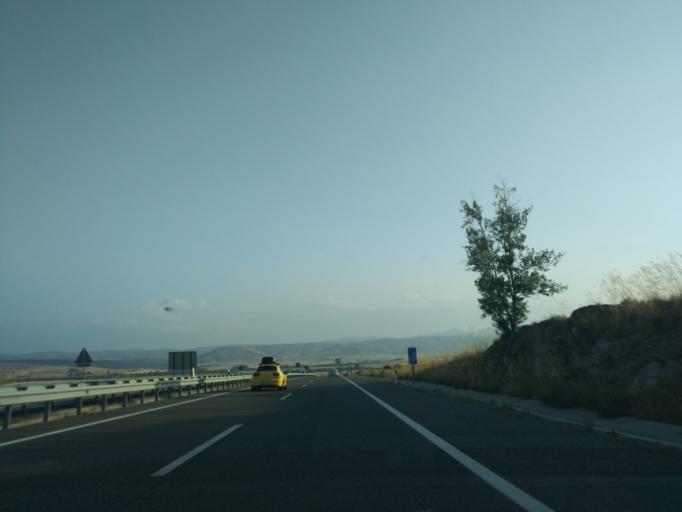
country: ES
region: Castille and Leon
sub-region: Provincia de Avila
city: Avila
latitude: 40.6566
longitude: -4.7231
